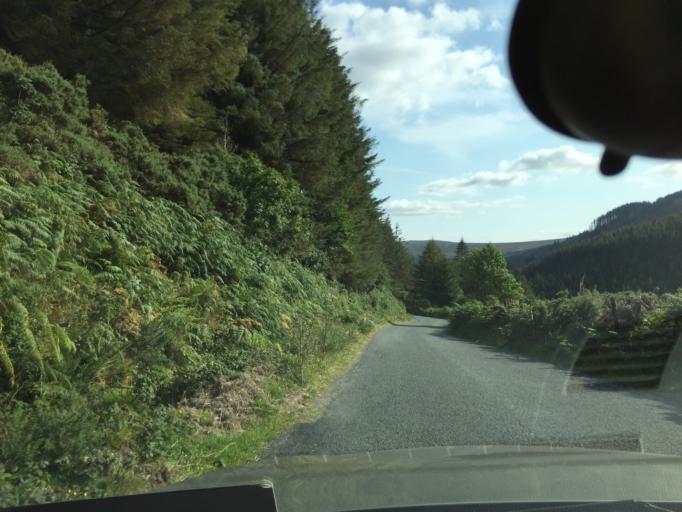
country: IE
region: Leinster
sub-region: Wicklow
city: Rathdrum
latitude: 53.0575
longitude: -6.3313
